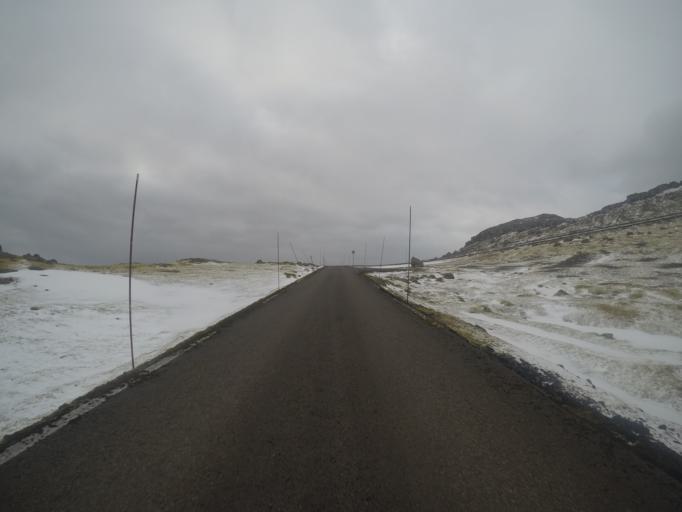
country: FO
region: Streymoy
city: Kollafjordhur
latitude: 62.0807
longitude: -6.9501
